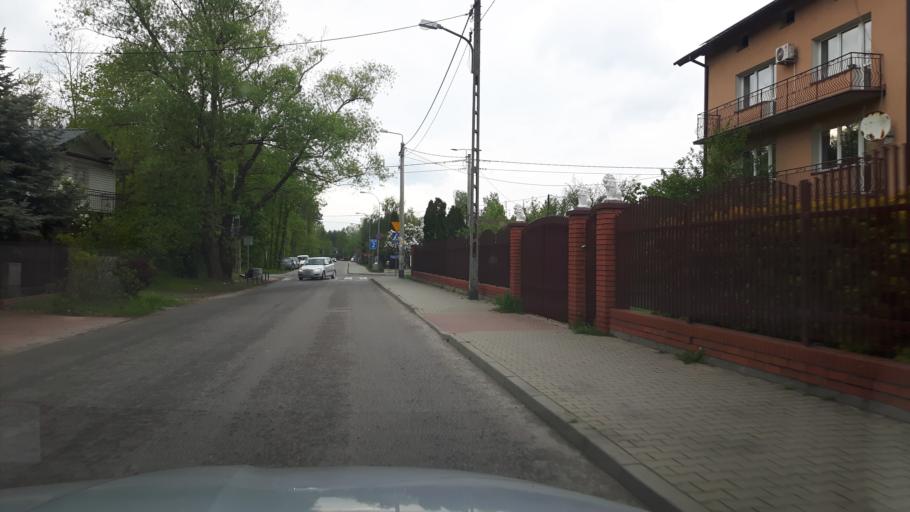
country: PL
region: Masovian Voivodeship
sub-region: Warszawa
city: Rembertow
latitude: 52.2724
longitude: 21.1576
